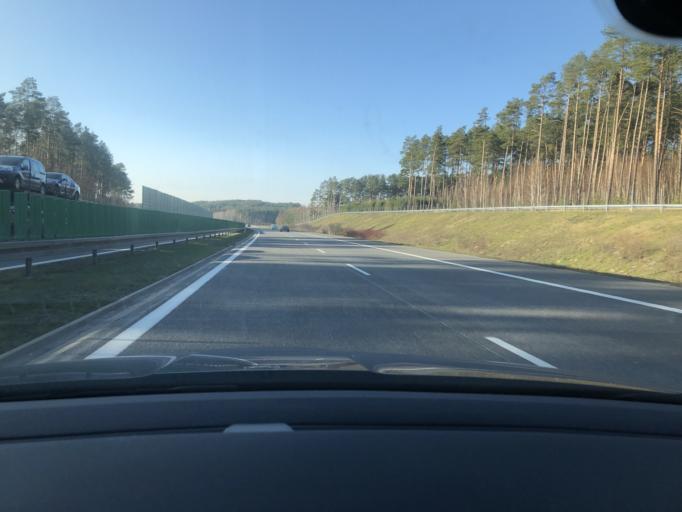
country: PL
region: Lubusz
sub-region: Powiat sulecinski
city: Torzym
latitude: 52.3315
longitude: 15.0272
